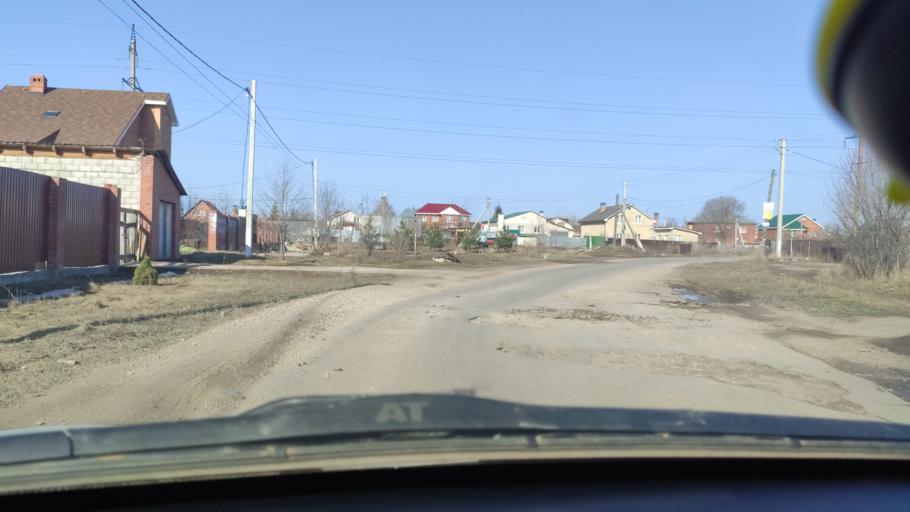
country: RU
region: Samara
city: Tol'yatti
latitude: 53.5582
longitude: 49.3885
